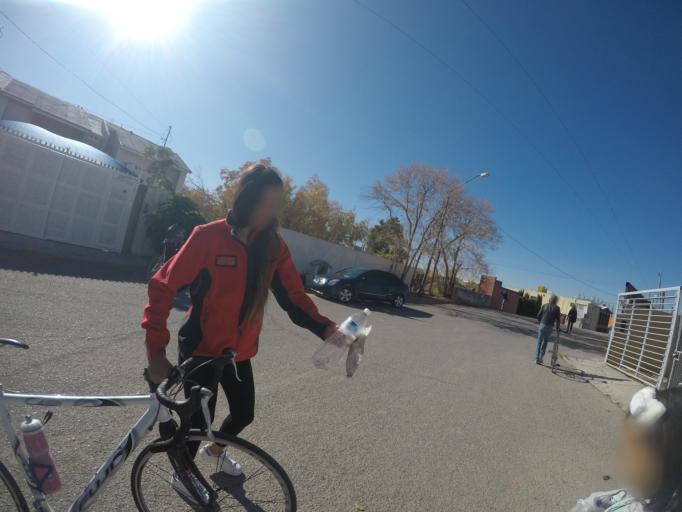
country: MX
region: Chihuahua
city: Ciudad Juarez
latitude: 31.7318
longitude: -106.4344
